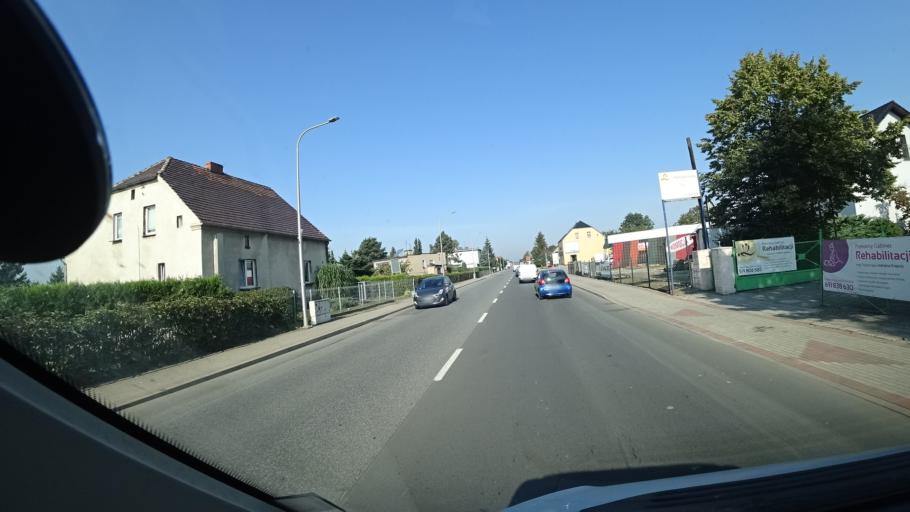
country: PL
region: Opole Voivodeship
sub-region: Powiat kedzierzynsko-kozielski
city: Kozle
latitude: 50.3412
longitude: 18.1747
